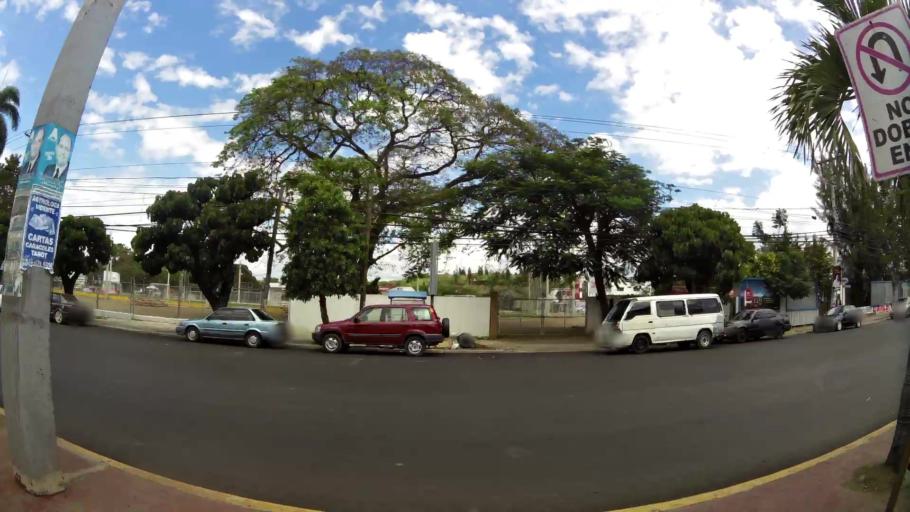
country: DO
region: Santiago
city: Santiago de los Caballeros
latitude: 19.4590
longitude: -70.6836
